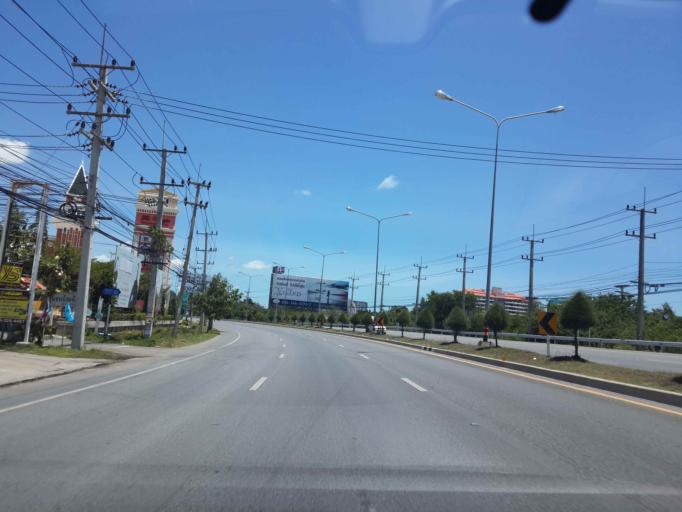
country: TH
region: Prachuap Khiri Khan
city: Hua Hin
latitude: 12.6493
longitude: 99.9514
